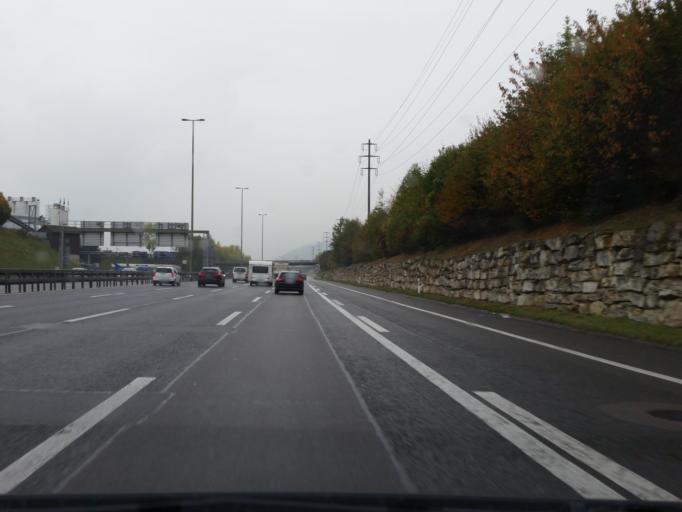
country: CH
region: Zurich
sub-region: Bezirk Dietikon
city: Geroldswil
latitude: 47.4141
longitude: 8.4227
